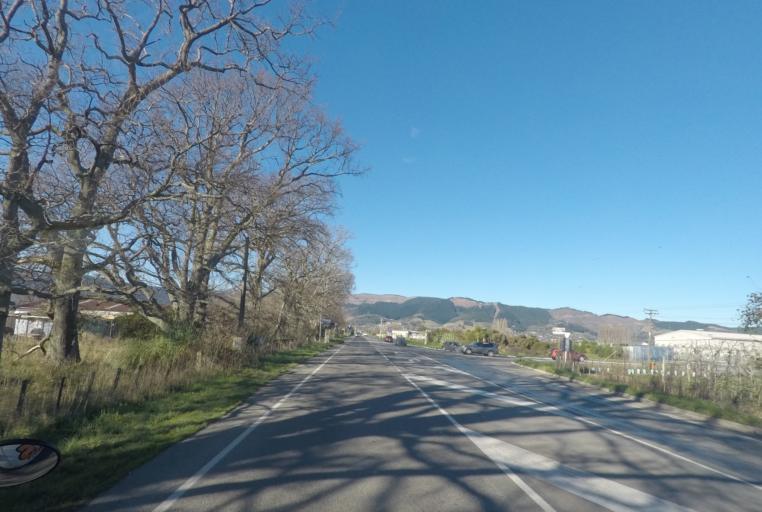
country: NZ
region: Tasman
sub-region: Tasman District
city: Richmond
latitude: -41.3265
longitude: 173.1706
